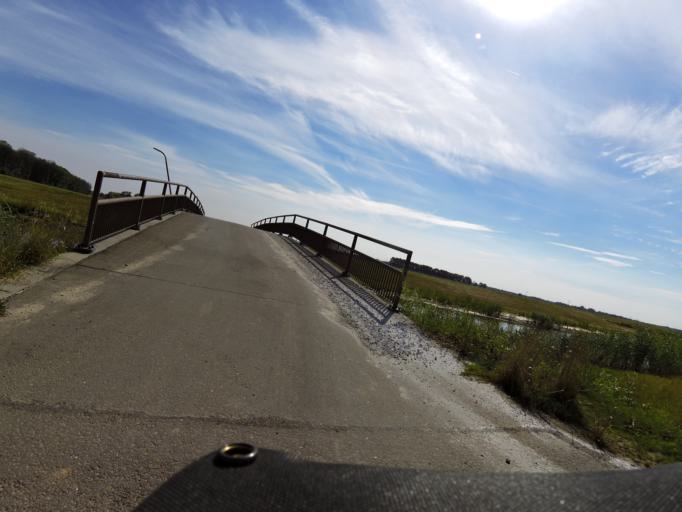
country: NL
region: South Holland
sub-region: Gemeente Hardinxveld-Giessendam
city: Neder-Hardinxveld
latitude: 51.7730
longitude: 4.8355
